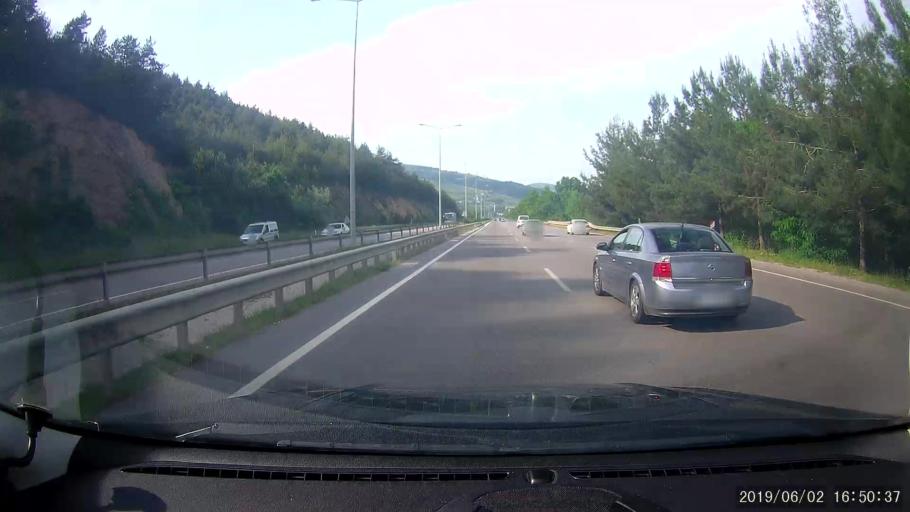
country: TR
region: Samsun
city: Taflan
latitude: 41.2582
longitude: 36.1741
